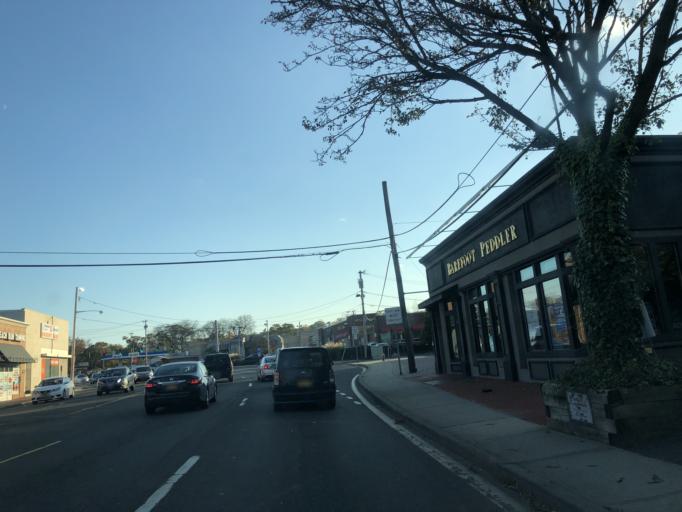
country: US
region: New York
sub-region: Nassau County
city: Greenvale
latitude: 40.8108
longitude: -73.6284
